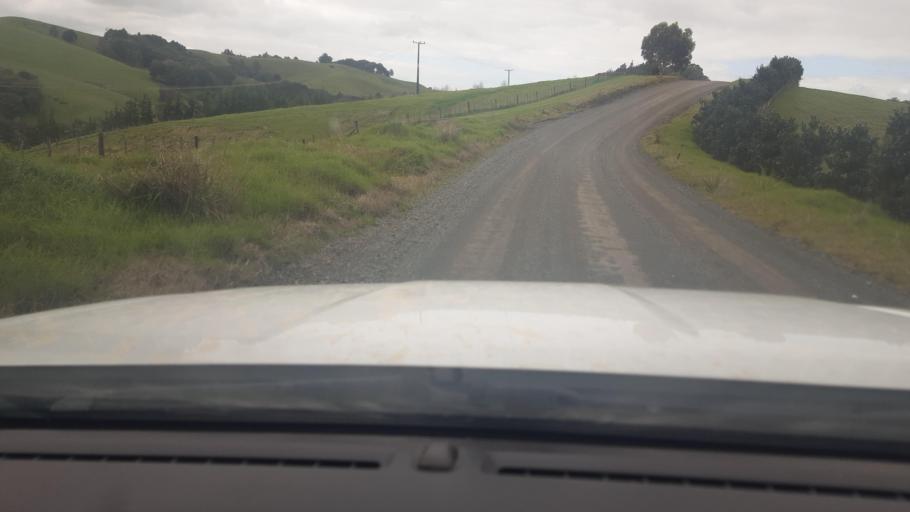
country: NZ
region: Northland
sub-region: Far North District
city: Kaitaia
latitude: -35.0921
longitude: 173.3149
